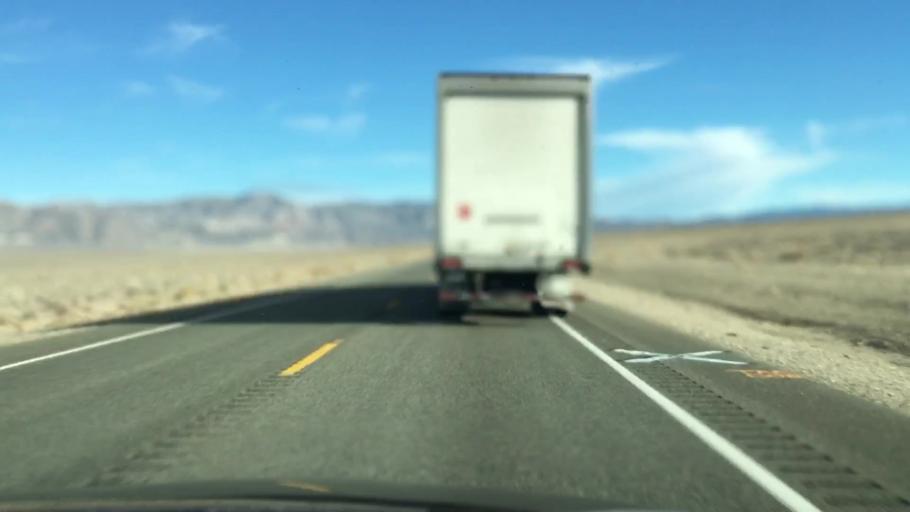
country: US
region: Nevada
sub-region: Mineral County
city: Hawthorne
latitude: 38.5307
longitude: -118.2692
